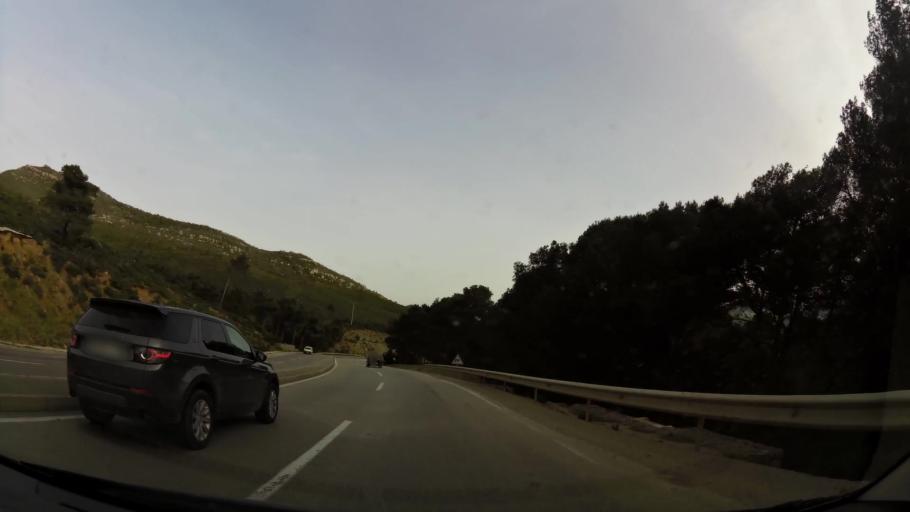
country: MA
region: Tanger-Tetouan
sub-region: Tetouan
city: Saddina
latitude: 35.5587
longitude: -5.5695
